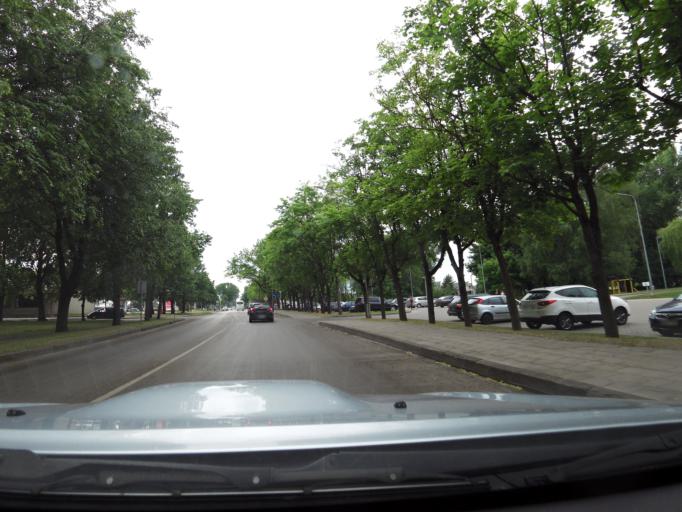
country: LT
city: Vilkaviskis
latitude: 54.6489
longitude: 23.0307
